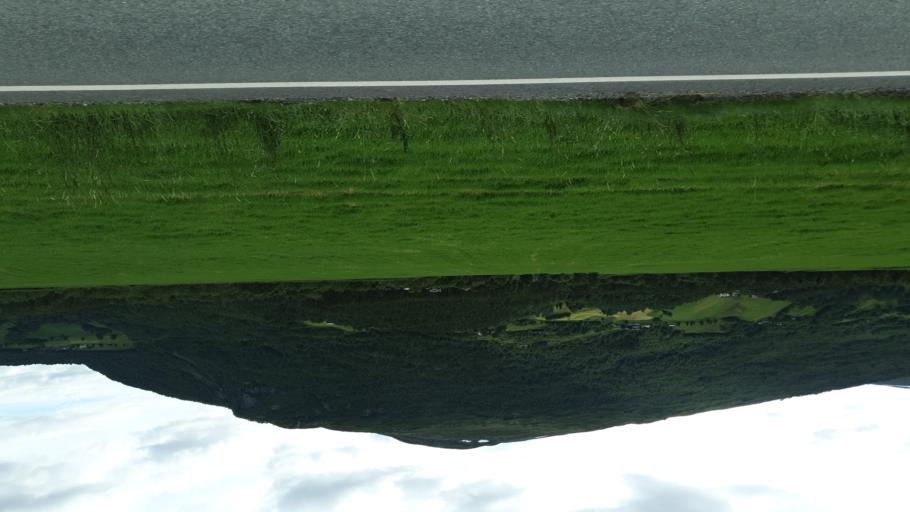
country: NO
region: Sor-Trondelag
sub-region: Oppdal
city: Oppdal
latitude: 62.5405
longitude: 9.6291
